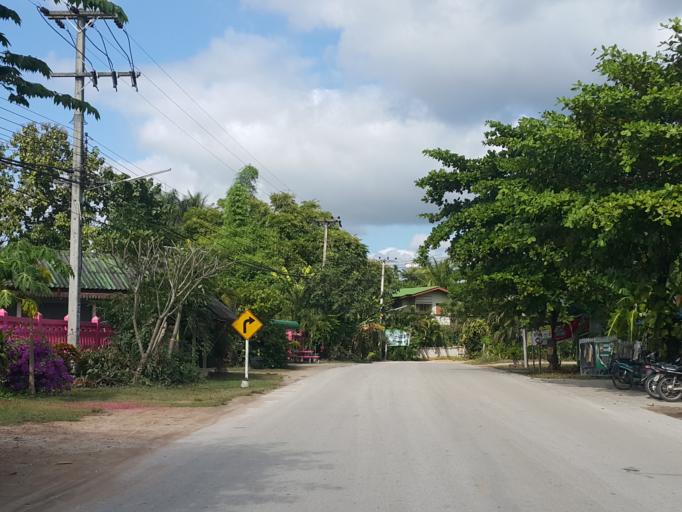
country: TH
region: Lampang
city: Hang Chat
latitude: 18.3363
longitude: 99.3554
